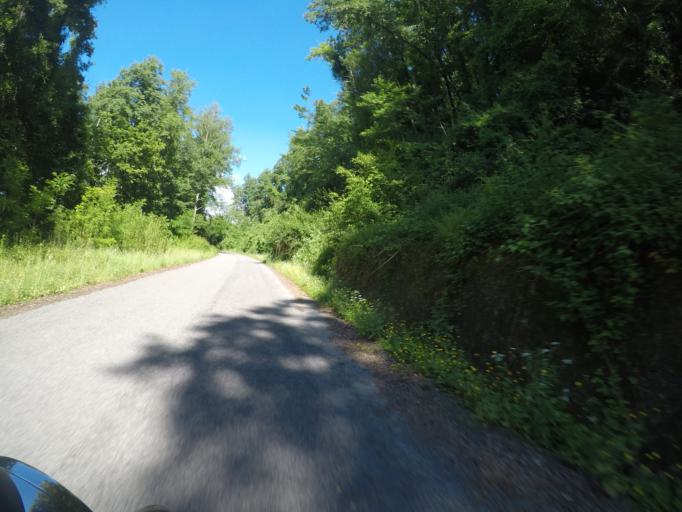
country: IT
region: Tuscany
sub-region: Provincia di Massa-Carrara
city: Fosdinovo
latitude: 44.1486
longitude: 10.0796
